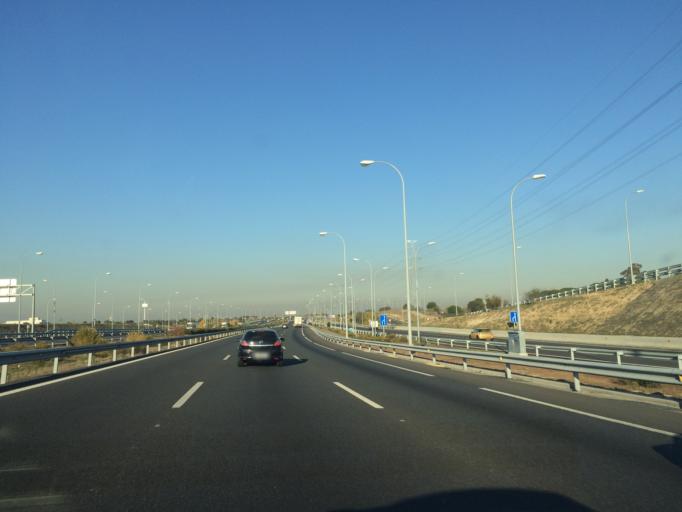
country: ES
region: Madrid
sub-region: Provincia de Madrid
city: Pozuelo de Alarcon
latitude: 40.4002
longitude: -3.8323
